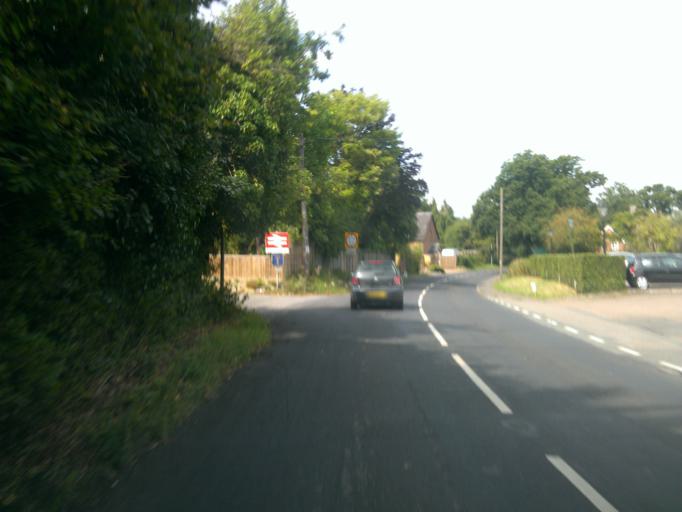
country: GB
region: England
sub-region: Kent
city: Sevenoaks
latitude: 51.1975
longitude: 0.1744
